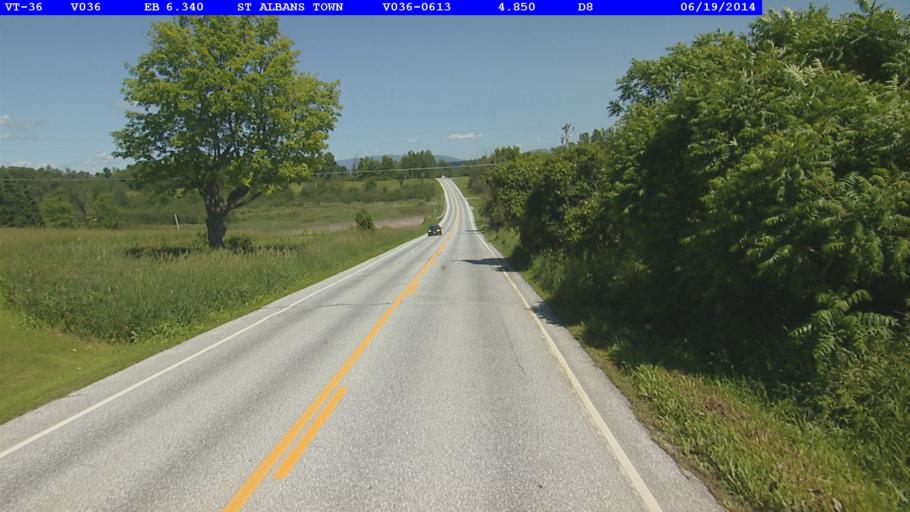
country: US
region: Vermont
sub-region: Franklin County
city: Saint Albans
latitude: 44.7904
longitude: -73.0393
